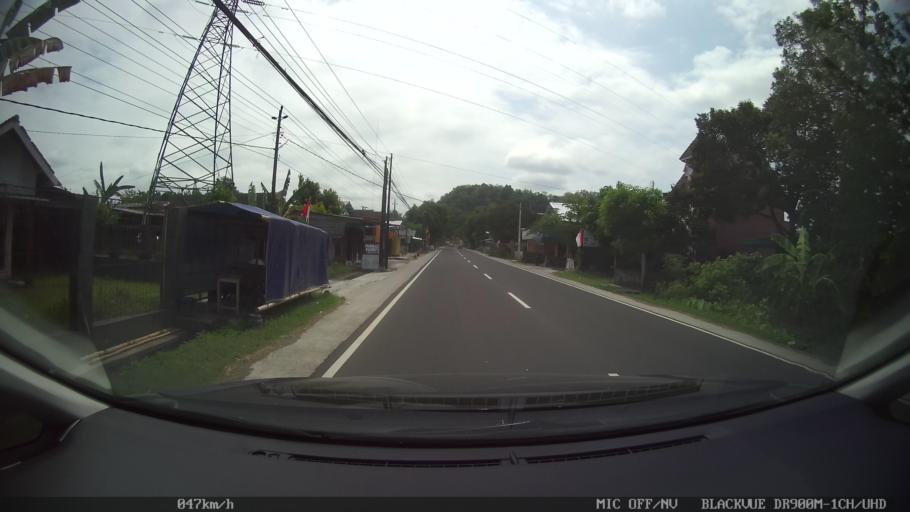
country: ID
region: Central Java
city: Candi Prambanan
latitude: -7.7807
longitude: 110.4826
